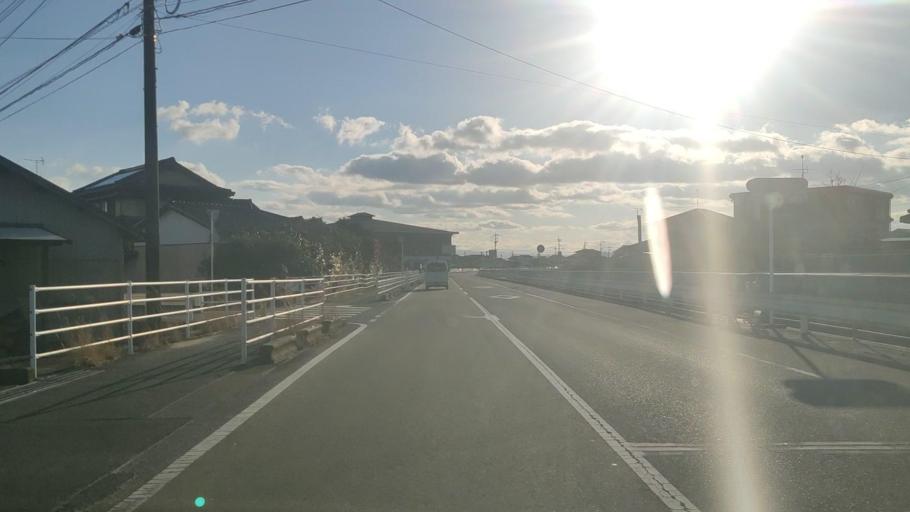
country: JP
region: Saga Prefecture
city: Saga-shi
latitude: 33.2756
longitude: 130.2223
